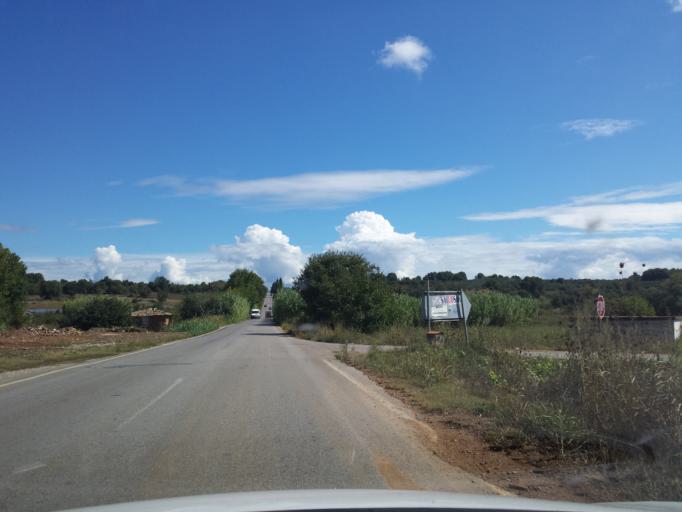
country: GR
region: Peloponnese
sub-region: Nomos Messinias
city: Vlakhopoulon
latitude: 36.9875
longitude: 21.8296
